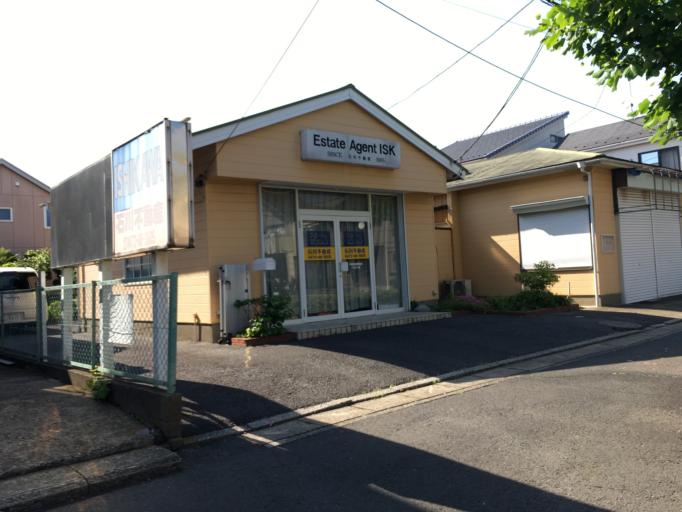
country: JP
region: Chiba
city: Matsudo
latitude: 35.8191
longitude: 139.9140
